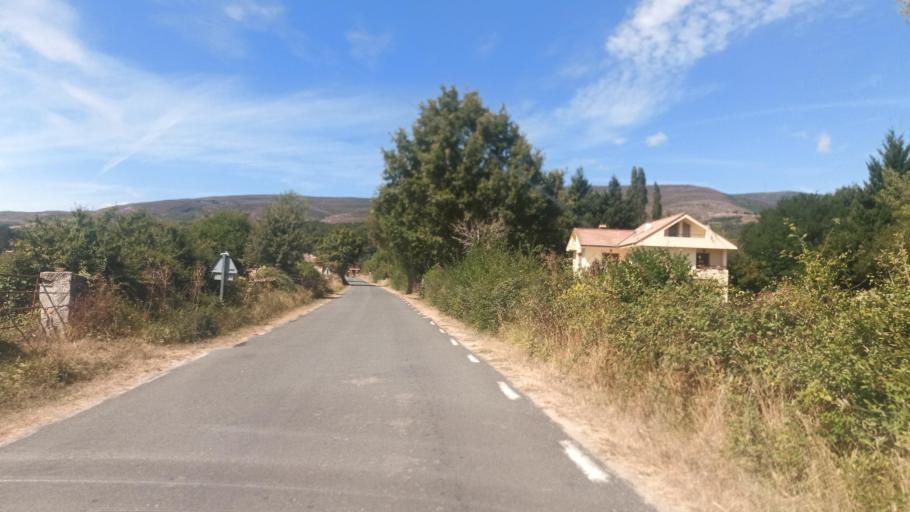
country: ES
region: Castille and Leon
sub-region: Provincia de Burgos
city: Espinosa de los Monteros
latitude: 43.0459
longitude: -3.6702
